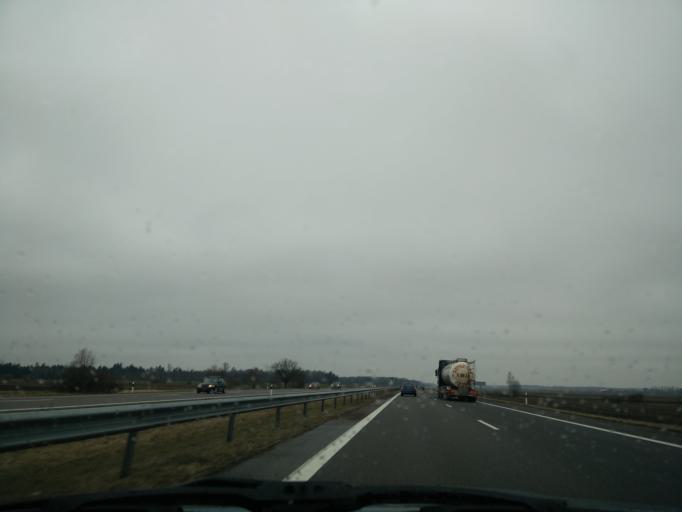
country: LT
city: Raseiniai
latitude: 55.3699
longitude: 22.9679
